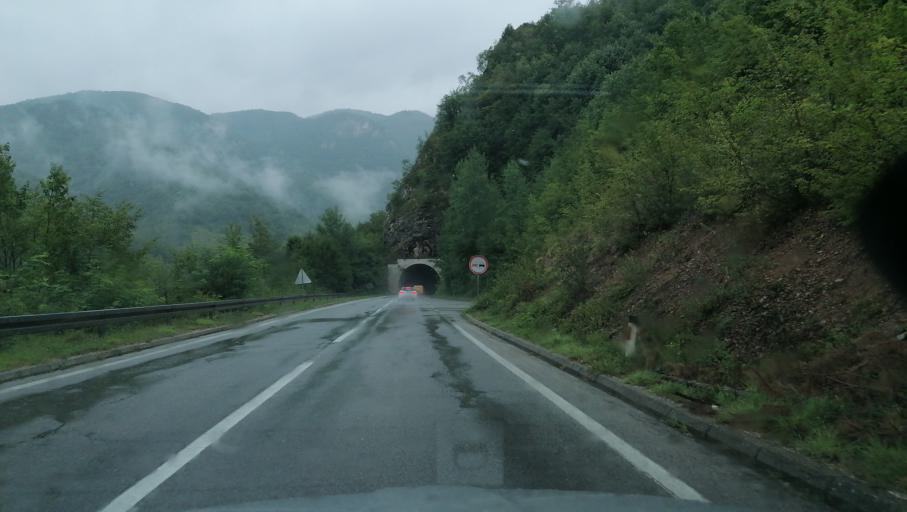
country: BA
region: Republika Srpska
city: Visegrad
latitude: 43.7016
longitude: 19.1705
